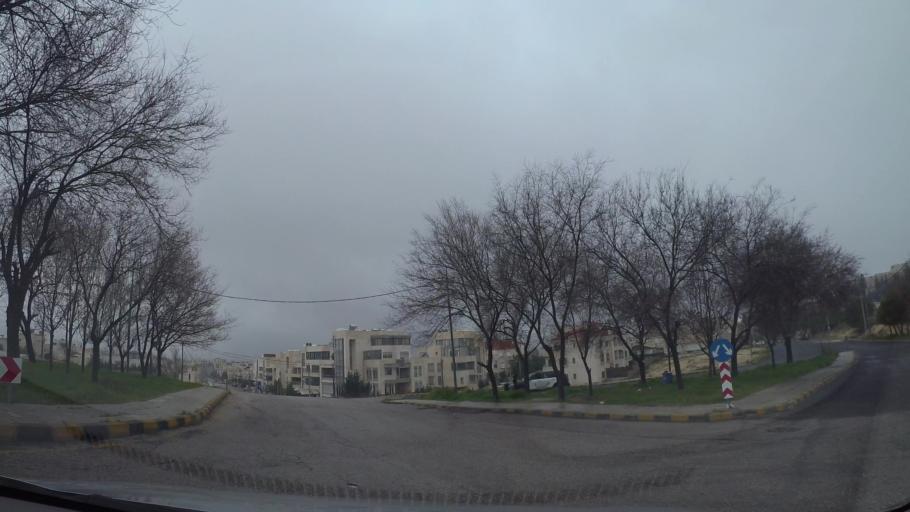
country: JO
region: Amman
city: Al Jubayhah
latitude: 32.0092
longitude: 35.8254
